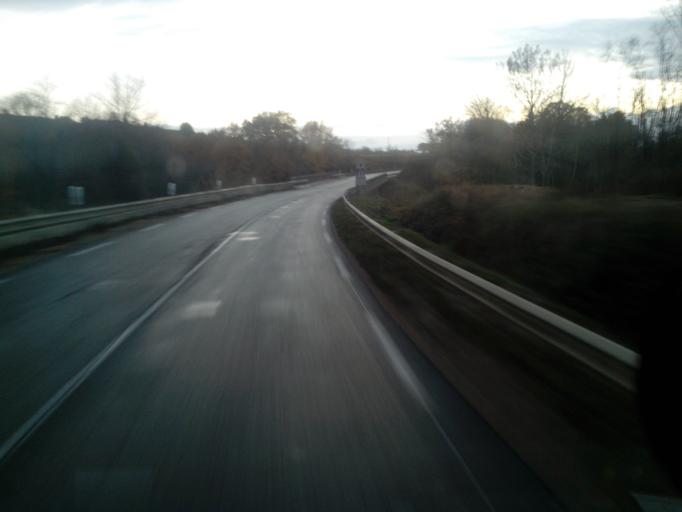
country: FR
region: Languedoc-Roussillon
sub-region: Departement de l'Herault
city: Gignac
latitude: 43.6643
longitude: 3.5660
